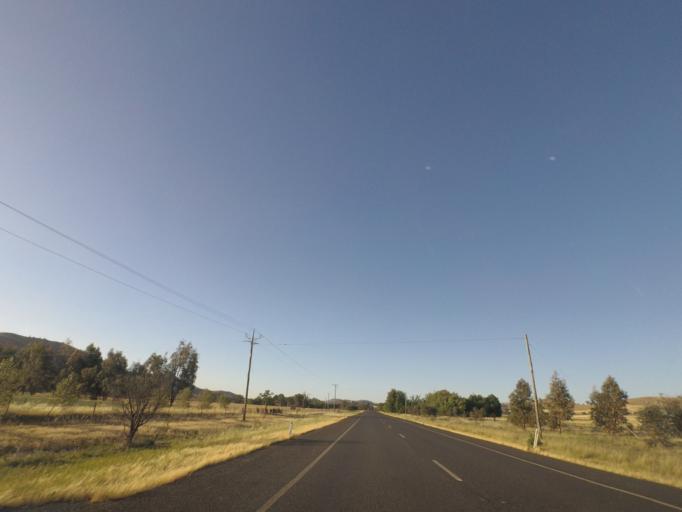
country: AU
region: New South Wales
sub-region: Gundagai
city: Gundagai
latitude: -34.9399
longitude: 148.1680
